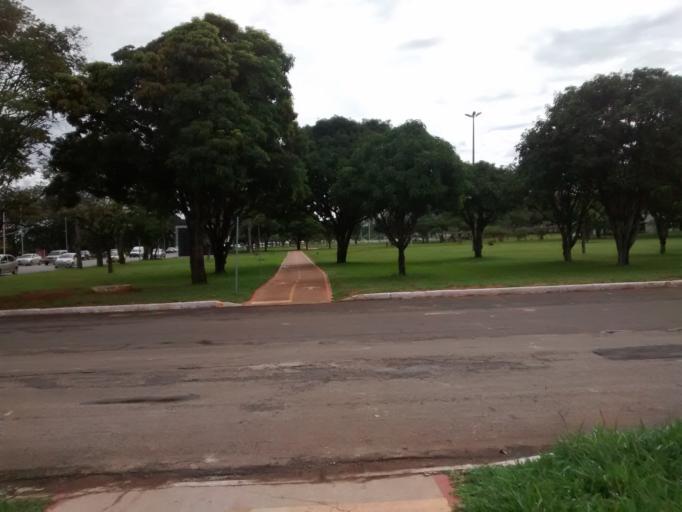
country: BR
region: Federal District
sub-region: Brasilia
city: Brasilia
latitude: -15.7911
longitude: -47.8964
